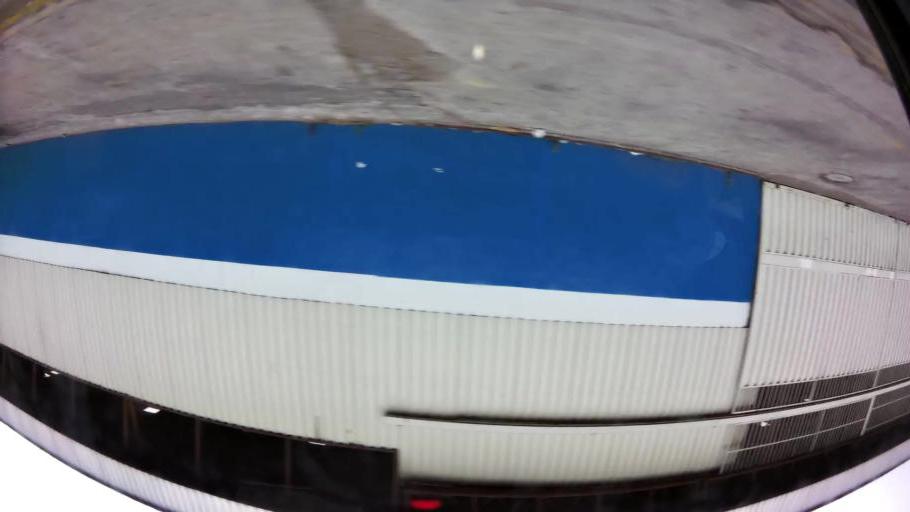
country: HN
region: Francisco Morazan
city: Tegucigalpa
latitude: 14.0808
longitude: -87.2030
